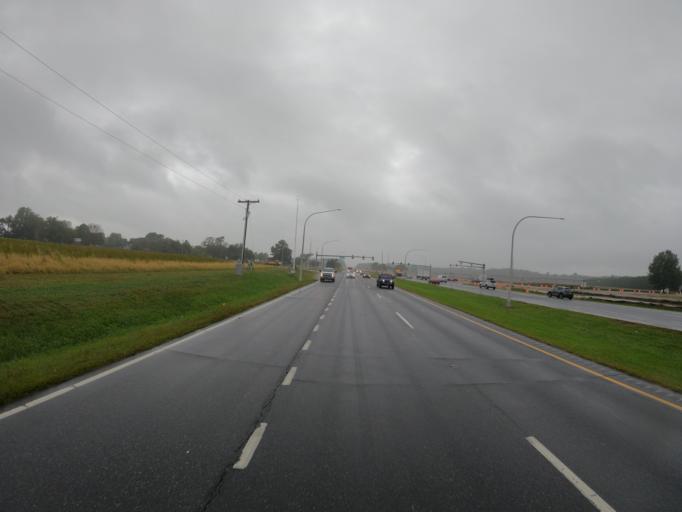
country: US
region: Delaware
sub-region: Sussex County
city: Milton
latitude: 38.8046
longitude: -75.2707
